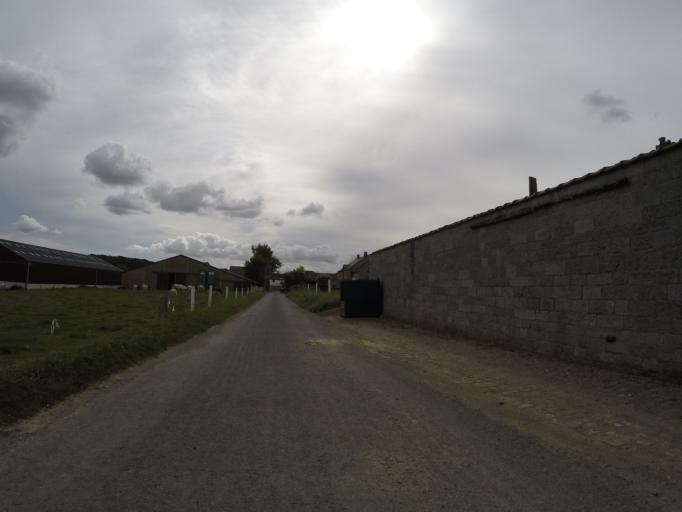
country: BE
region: Wallonia
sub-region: Province de Namur
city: Dinant
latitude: 50.2821
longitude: 4.9871
